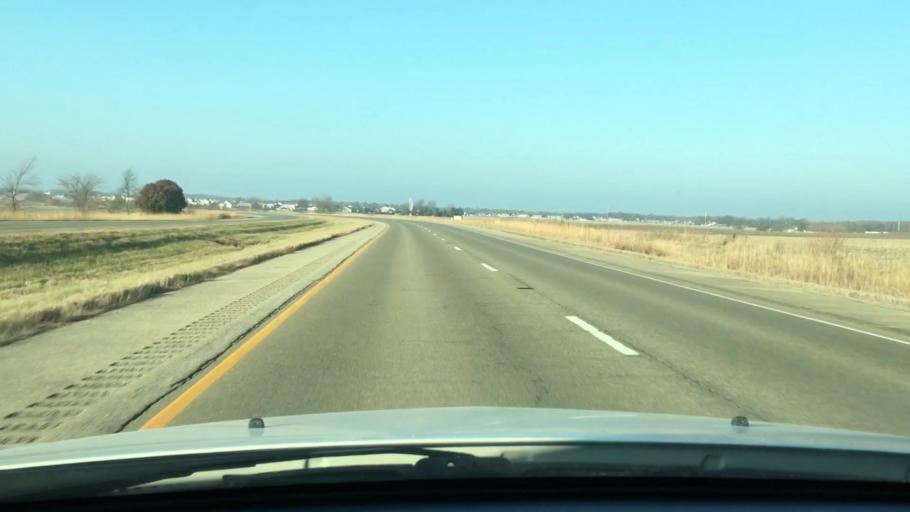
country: US
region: Illinois
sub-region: Tazewell County
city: Washington
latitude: 40.7276
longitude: -89.4188
